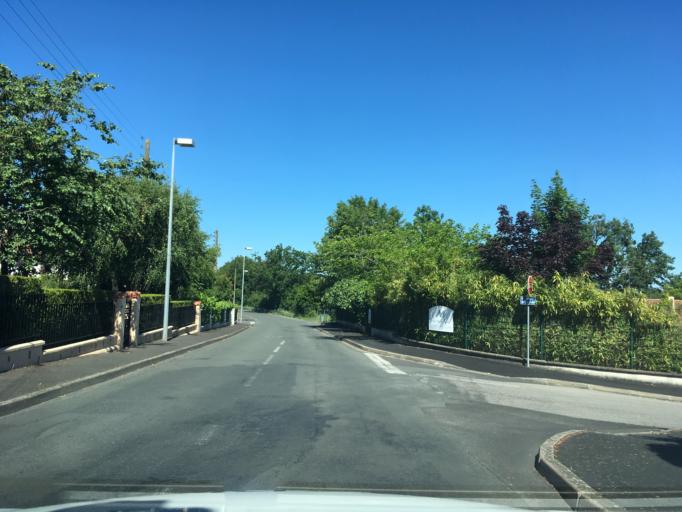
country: FR
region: Poitou-Charentes
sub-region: Departement des Deux-Sevres
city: Niort
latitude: 46.3279
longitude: -0.4323
